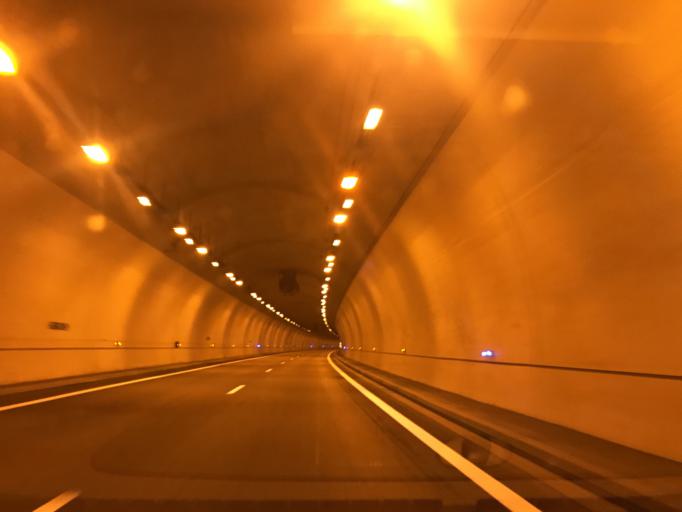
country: FR
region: Rhone-Alpes
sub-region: Departement de la Savoie
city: Aiton
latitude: 45.5392
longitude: 6.3038
